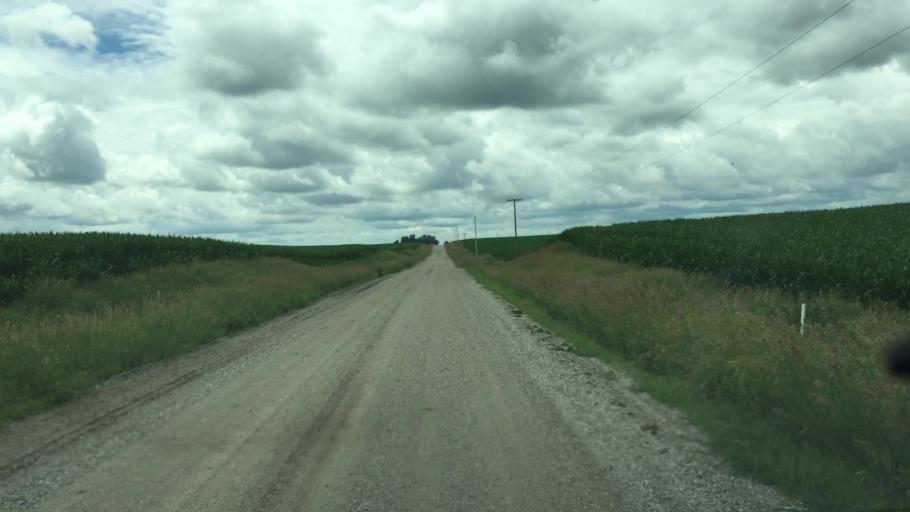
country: US
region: Iowa
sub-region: Jasper County
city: Prairie City
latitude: 41.5872
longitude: -93.1596
